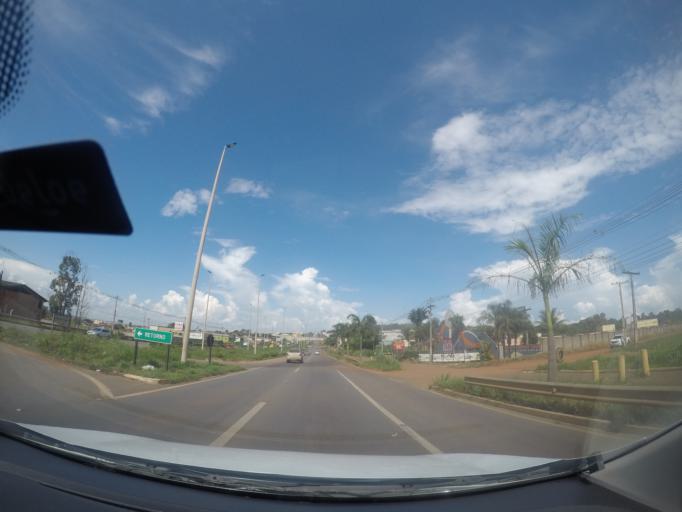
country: BR
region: Goias
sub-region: Goiania
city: Goiania
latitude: -16.6594
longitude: -49.3610
